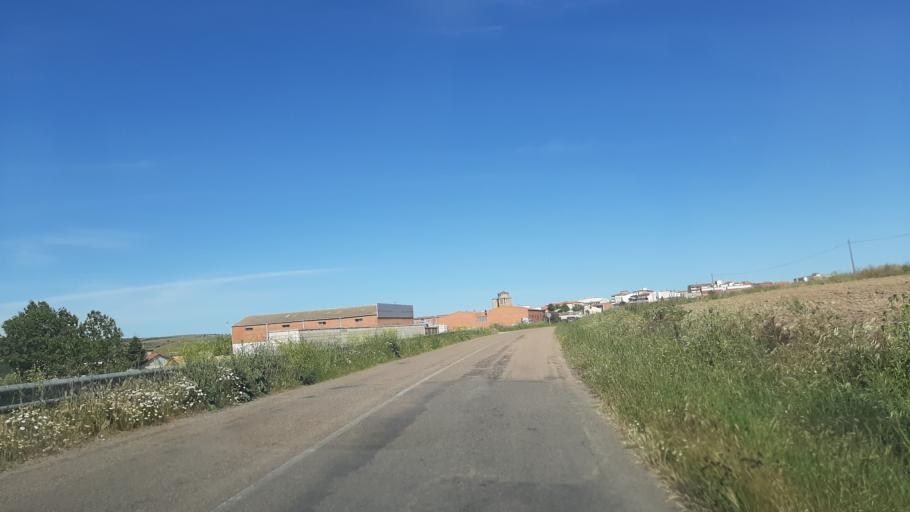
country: ES
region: Castille and Leon
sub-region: Provincia de Salamanca
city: Alba de Tormes
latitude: 40.8208
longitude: -5.5035
